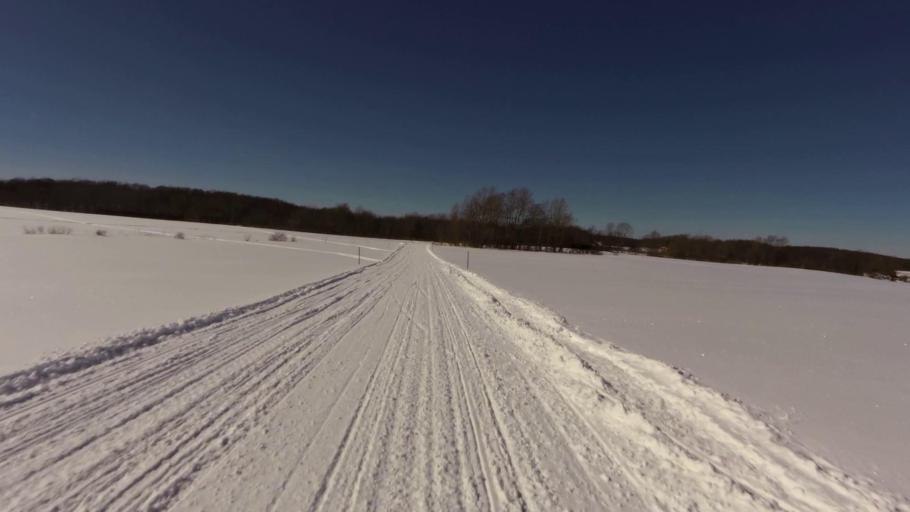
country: US
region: New York
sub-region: Chautauqua County
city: Lakewood
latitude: 42.2255
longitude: -79.3354
